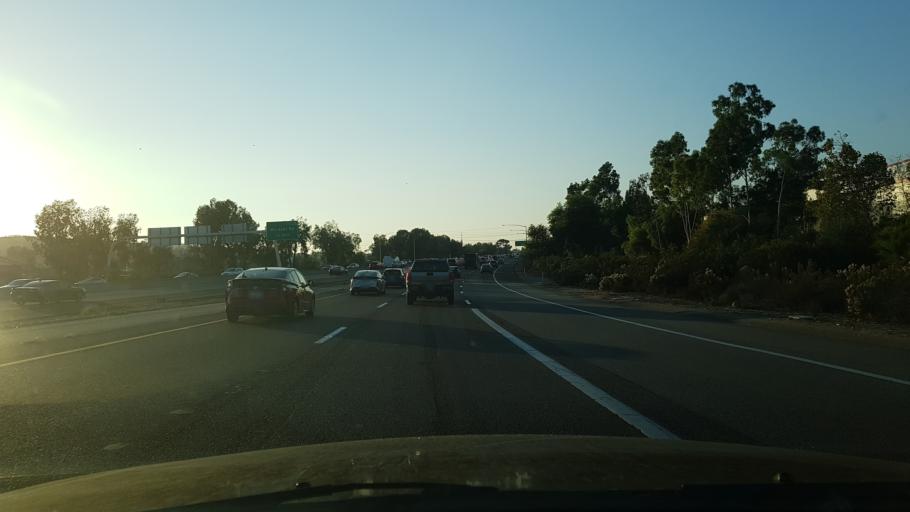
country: US
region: California
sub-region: San Diego County
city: Escondido
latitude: 33.1276
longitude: -117.1099
